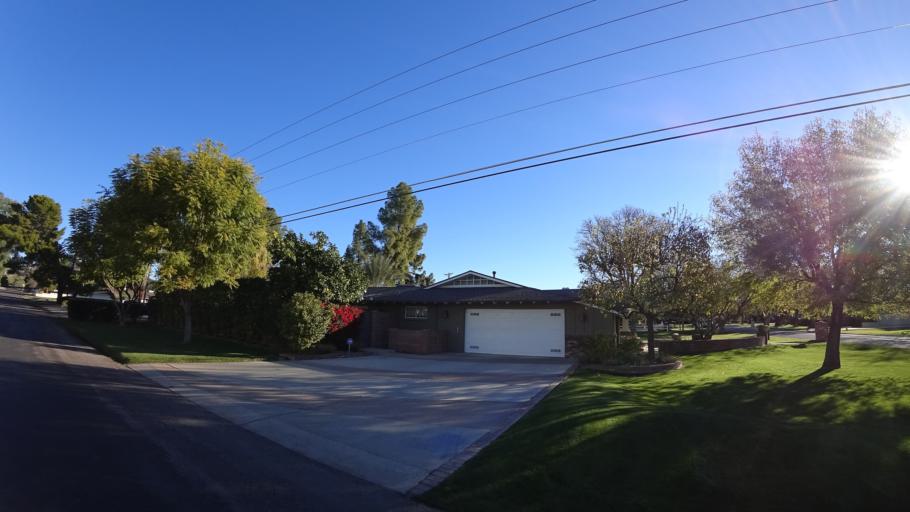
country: US
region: Arizona
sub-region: Maricopa County
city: Paradise Valley
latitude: 33.5123
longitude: -112.0041
